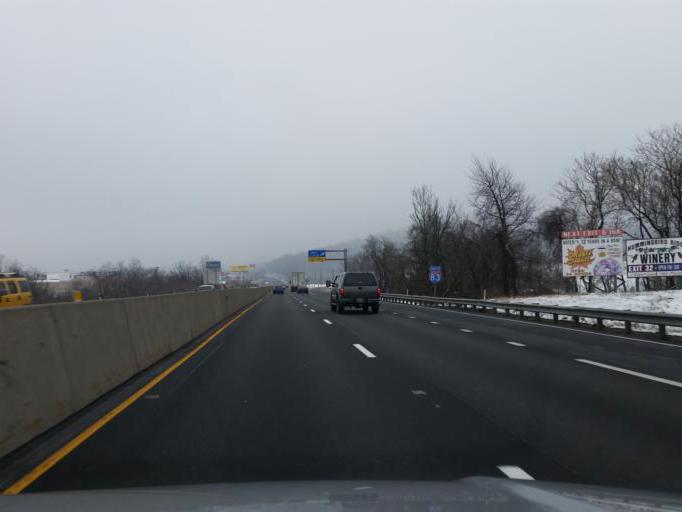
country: US
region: Pennsylvania
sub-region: York County
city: Valley Green
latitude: 40.1595
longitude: -76.8247
